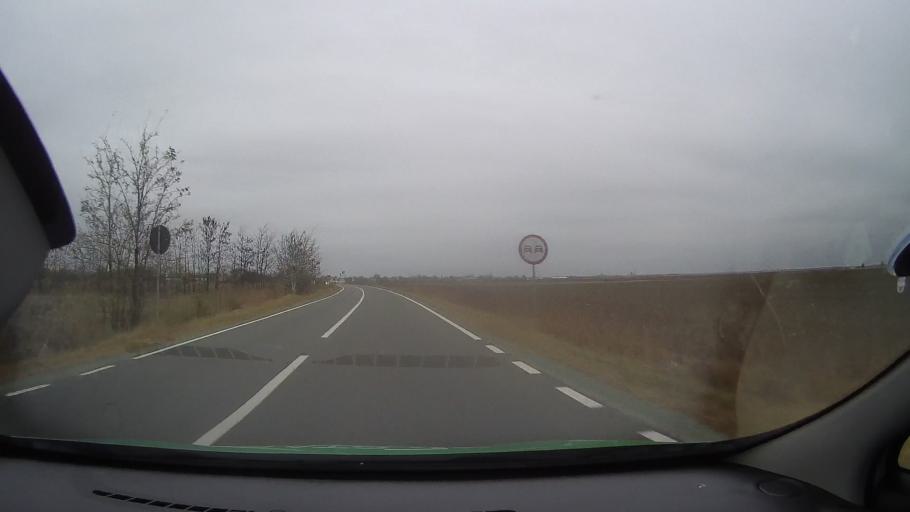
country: RO
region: Ialomita
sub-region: Comuna Slobozia
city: Slobozia
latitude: 44.6114
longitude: 27.3854
